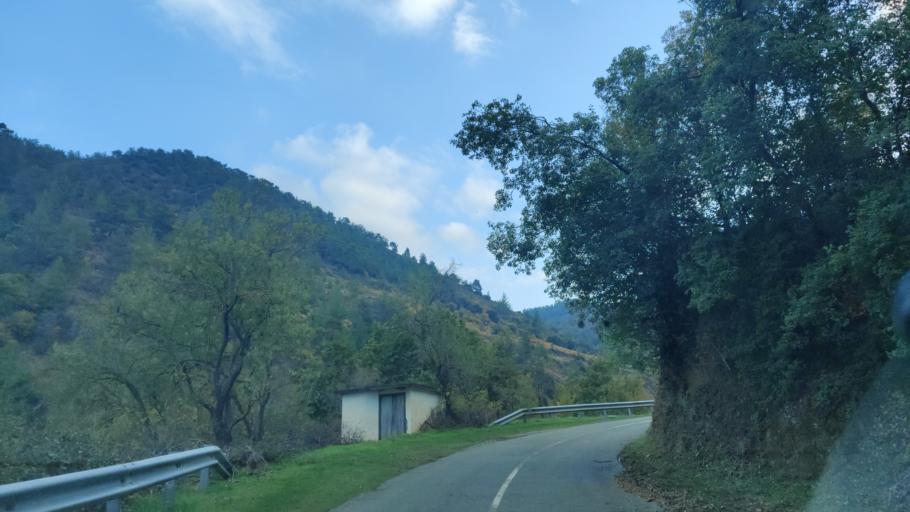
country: CY
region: Lefkosia
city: Lefka
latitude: 35.0493
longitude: 32.7358
